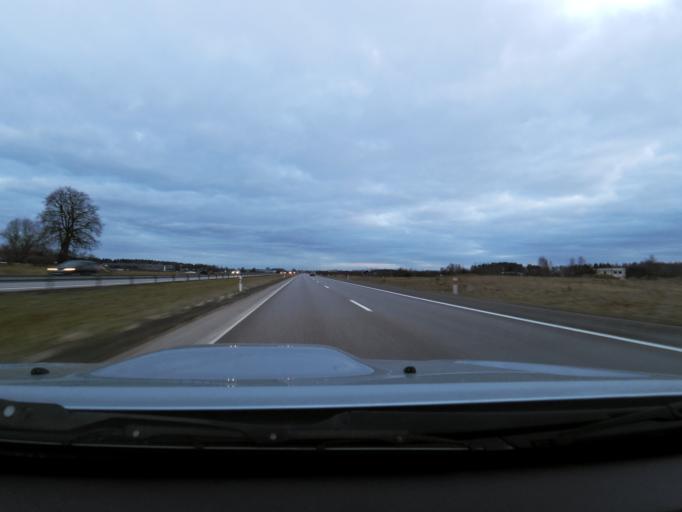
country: LT
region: Vilnius County
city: Pasilaiciai
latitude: 54.7803
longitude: 25.1832
